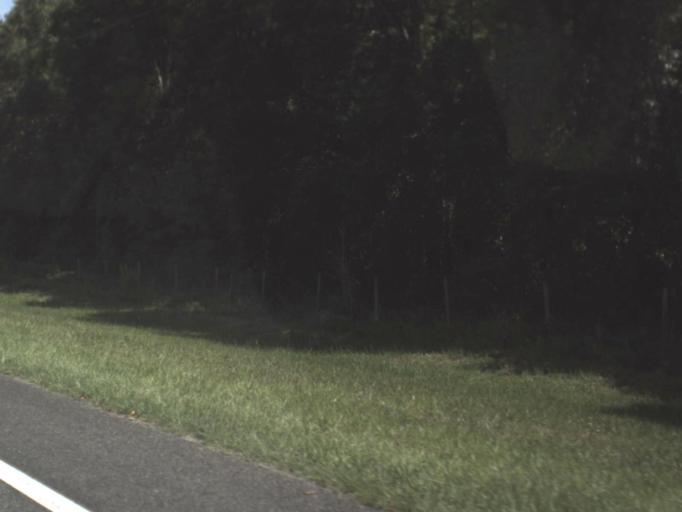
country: US
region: Florida
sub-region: Levy County
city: Manatee Road
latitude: 29.5478
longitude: -82.8983
